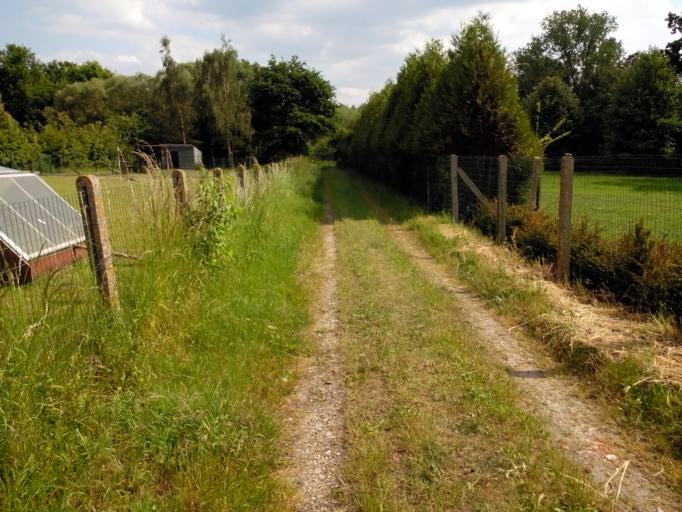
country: BE
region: Flanders
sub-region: Provincie Vlaams-Brabant
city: Rotselaar
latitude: 50.9731
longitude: 4.7223
